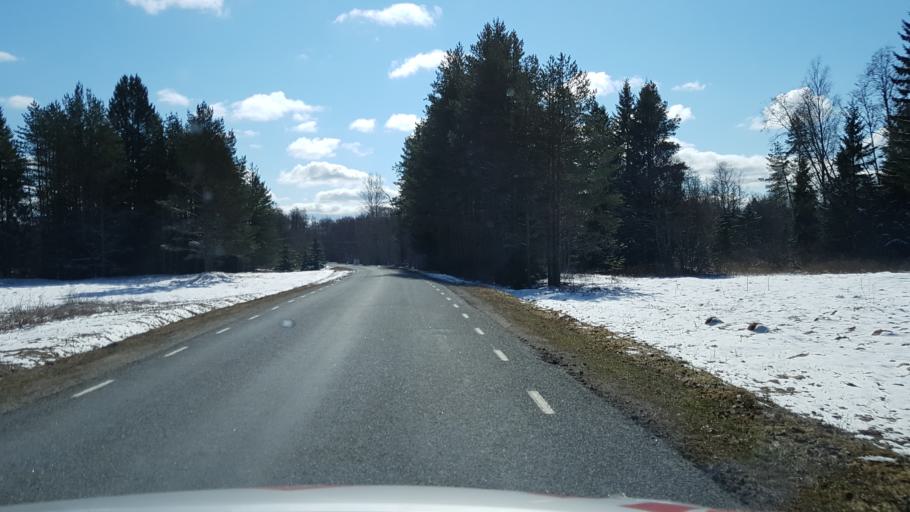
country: EE
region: Laeaene-Virumaa
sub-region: Tapa vald
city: Tapa
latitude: 59.4989
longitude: 25.9695
